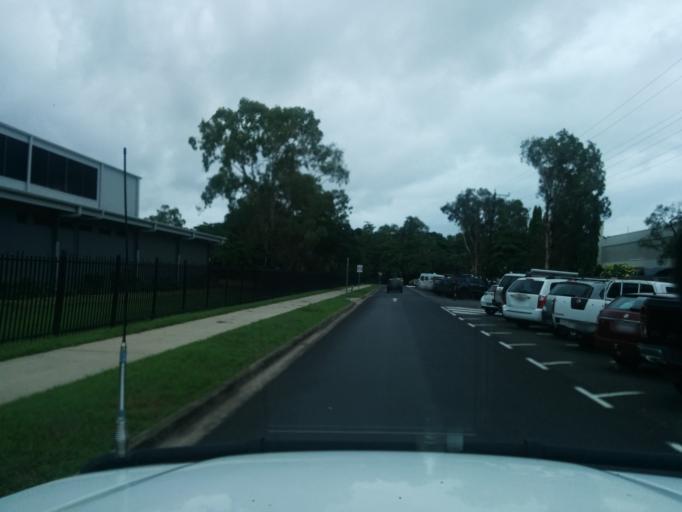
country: AU
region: Queensland
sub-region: Cairns
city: Cairns
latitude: -16.9212
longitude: 145.7537
